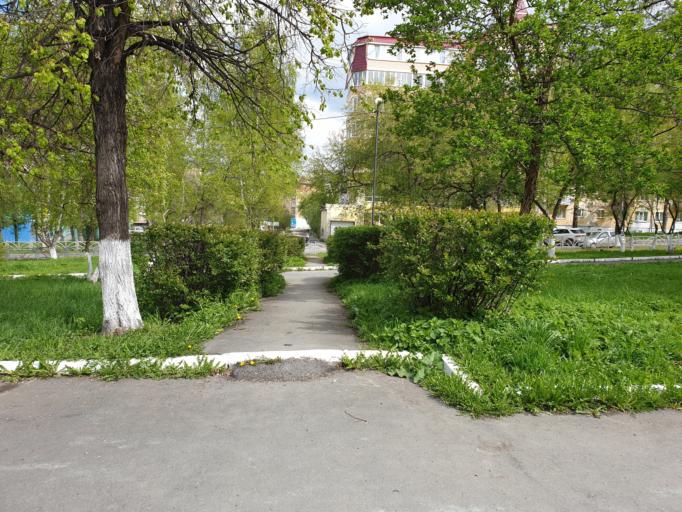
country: RU
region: Sverdlovsk
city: Pervoural'sk
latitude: 56.9113
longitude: 59.9438
